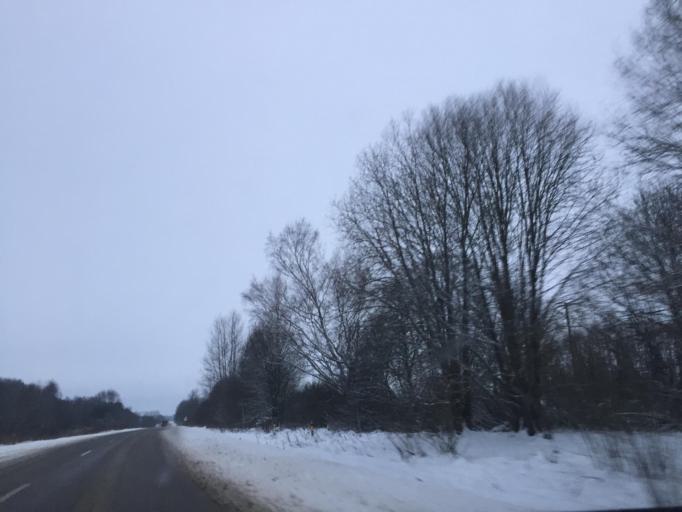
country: LV
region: Smiltene
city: Smiltene
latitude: 57.4285
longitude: 25.8531
